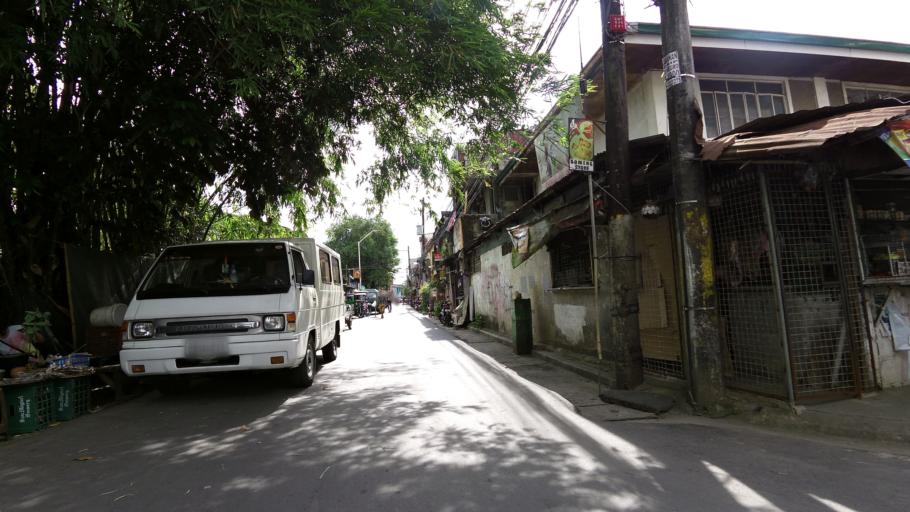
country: PH
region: Calabarzon
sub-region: Province of Rizal
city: Cainta
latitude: 14.5736
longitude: 121.1200
